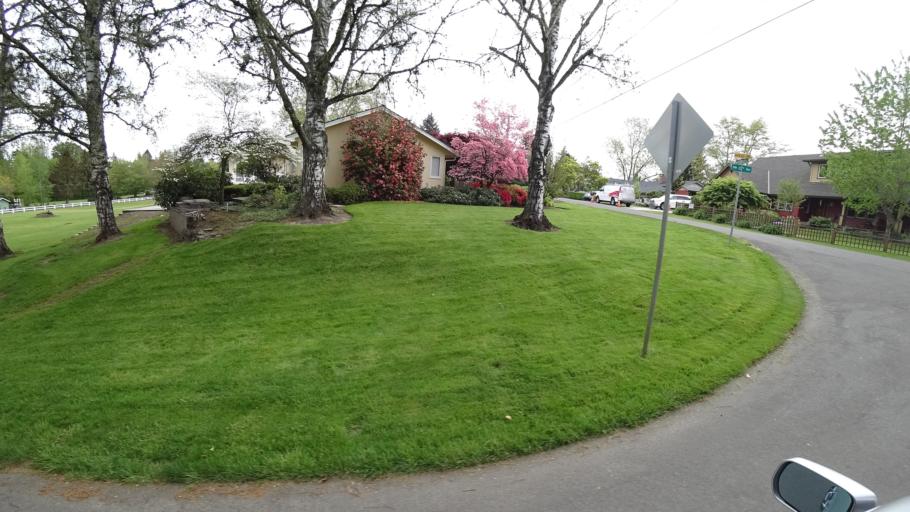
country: US
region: Oregon
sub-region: Washington County
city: Hillsboro
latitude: 45.5282
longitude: -123.0034
